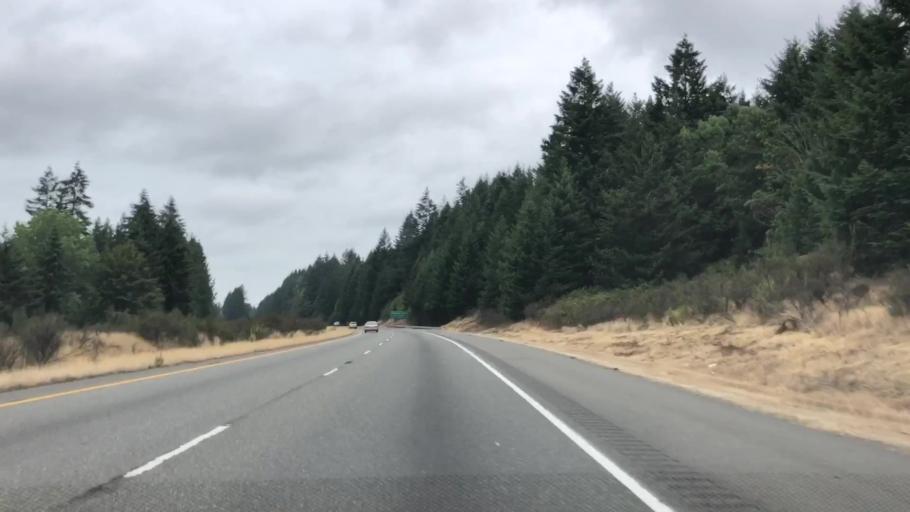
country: US
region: Washington
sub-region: Kitsap County
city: Burley
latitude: 47.4518
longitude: -122.6213
